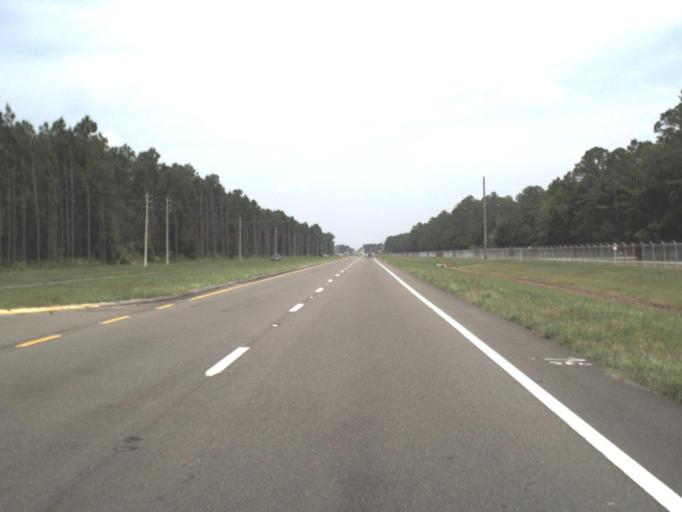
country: US
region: Florida
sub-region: Duval County
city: Baldwin
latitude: 30.2464
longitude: -81.8676
